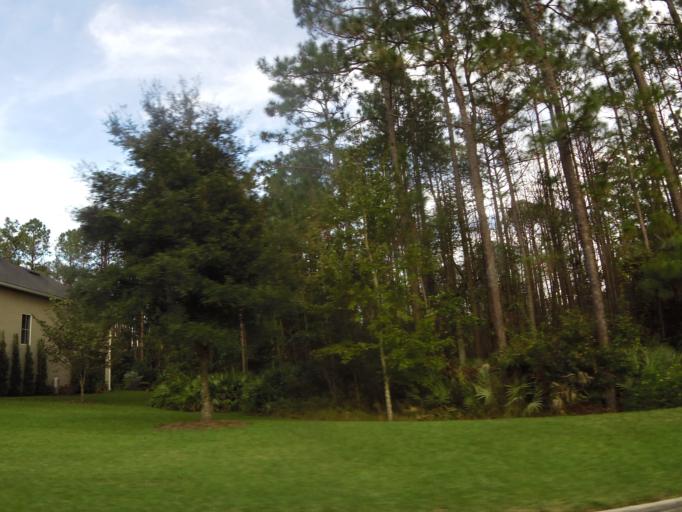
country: US
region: Florida
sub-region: Saint Johns County
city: Fruit Cove
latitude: 30.1502
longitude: -81.5385
